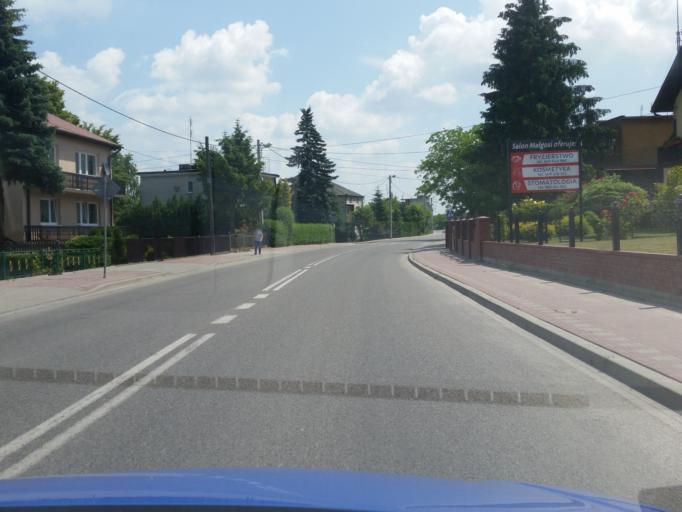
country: PL
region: Swietokrzyskie
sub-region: Powiat kazimierski
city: Skalbmierz
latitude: 50.3171
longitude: 20.4004
